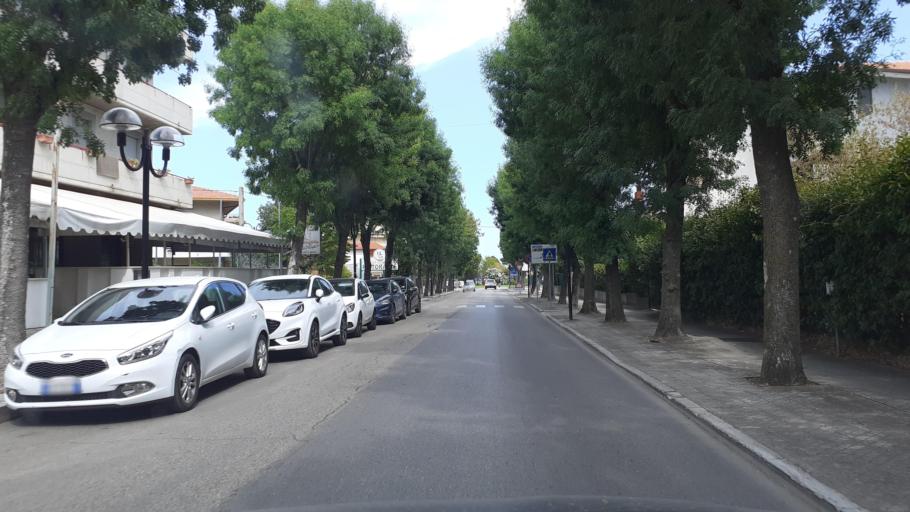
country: IT
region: Abruzzo
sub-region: Provincia di Chieti
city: Fossacesia
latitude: 42.2475
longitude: 14.4829
